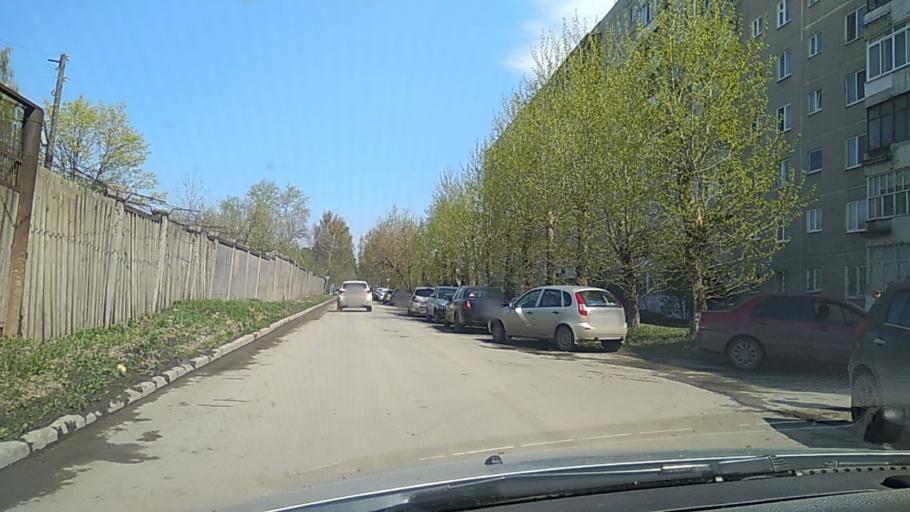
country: RU
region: Sverdlovsk
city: Verkhnyaya Pyshma
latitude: 56.9113
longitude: 60.5843
